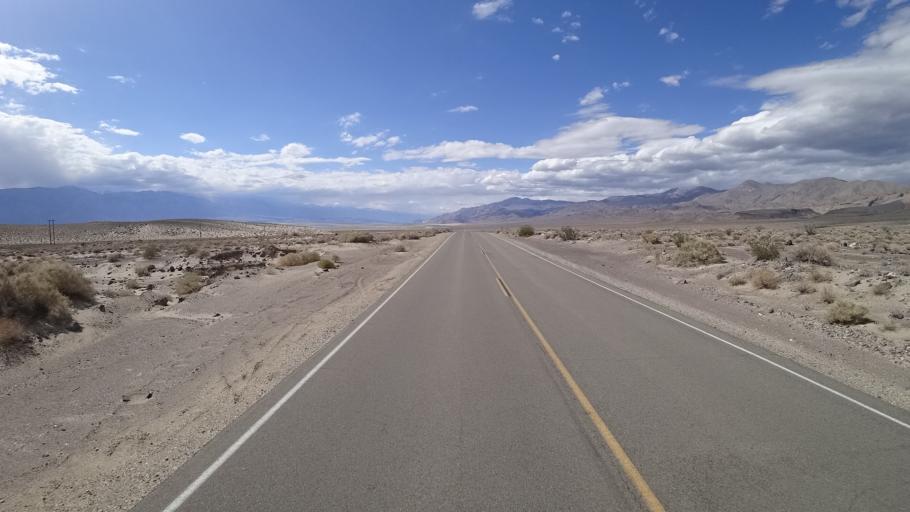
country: US
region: California
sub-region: Inyo County
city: Lone Pine
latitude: 36.4194
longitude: -117.8169
